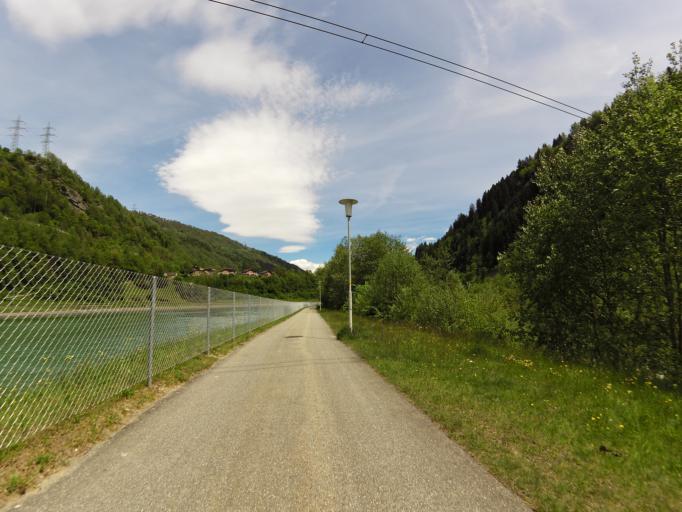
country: CH
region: Grisons
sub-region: Surselva District
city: Breil
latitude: 46.7519
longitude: 9.0464
